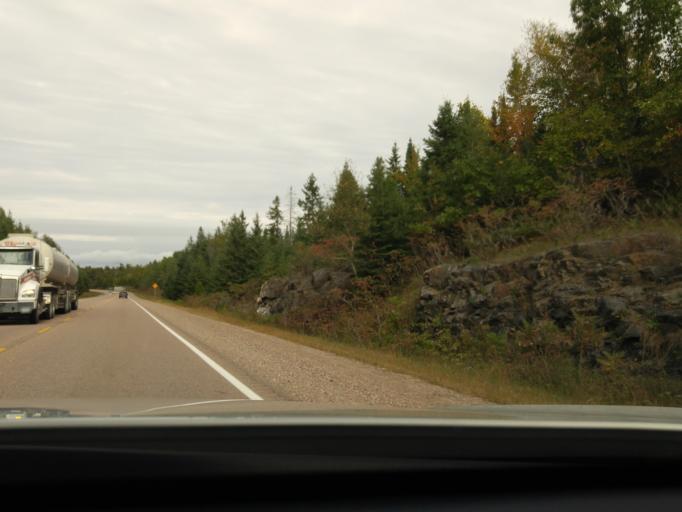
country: CA
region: Ontario
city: Renfrew
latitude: 45.5481
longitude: -76.7304
